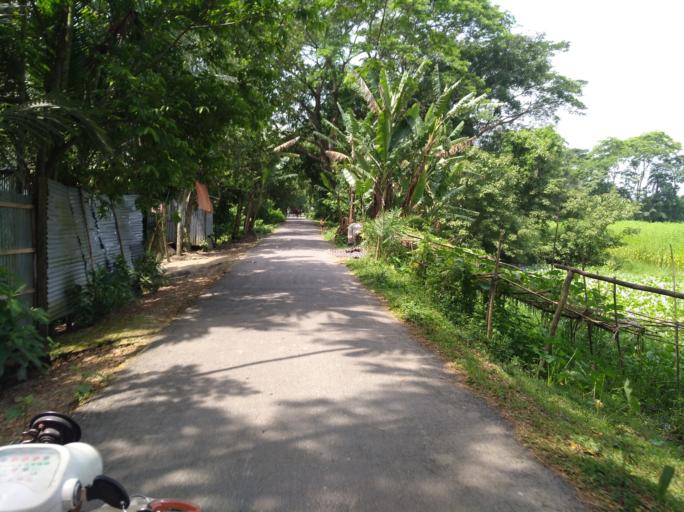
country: BD
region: Dhaka
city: Palang
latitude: 23.2524
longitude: 90.3107
